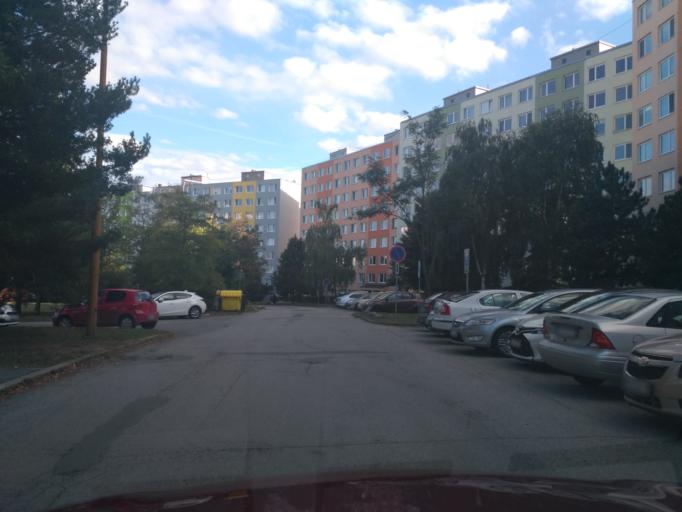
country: SK
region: Kosicky
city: Kosice
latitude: 48.7103
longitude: 21.2109
